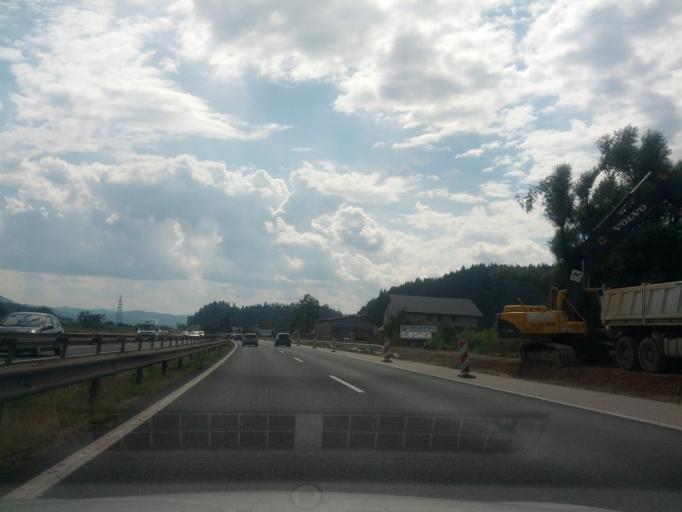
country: SI
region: Log-Dragomer
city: Dragomer
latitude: 46.0162
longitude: 14.3853
